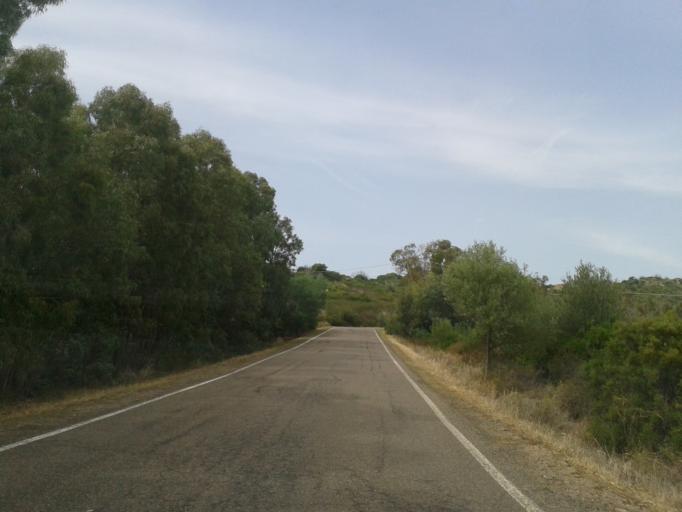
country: IT
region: Sardinia
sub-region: Provincia di Cagliari
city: Olia Speciosa
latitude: 39.2768
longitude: 9.5775
